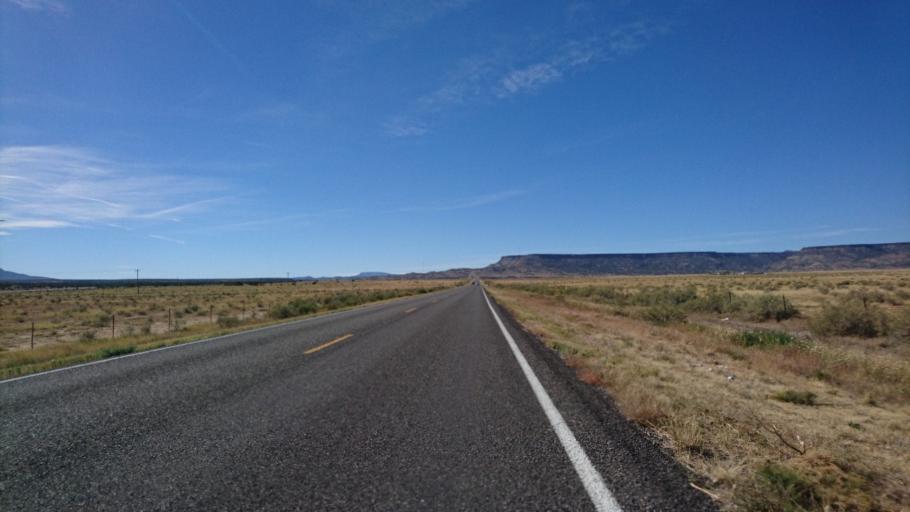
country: US
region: New Mexico
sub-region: Cibola County
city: Skyline-Ganipa
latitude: 35.0825
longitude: -107.6127
